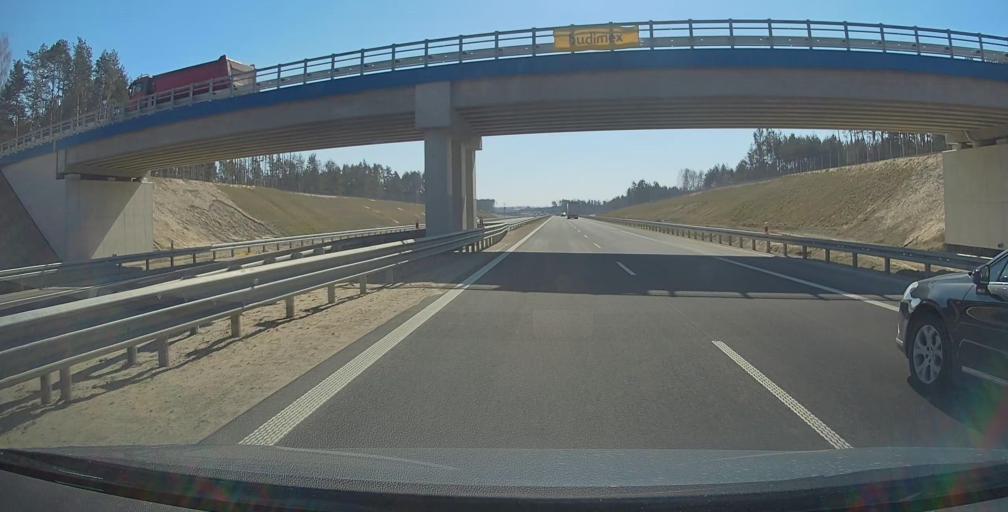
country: PL
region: Subcarpathian Voivodeship
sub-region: Powiat rzeszowski
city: Gorno
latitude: 50.2751
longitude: 22.1154
